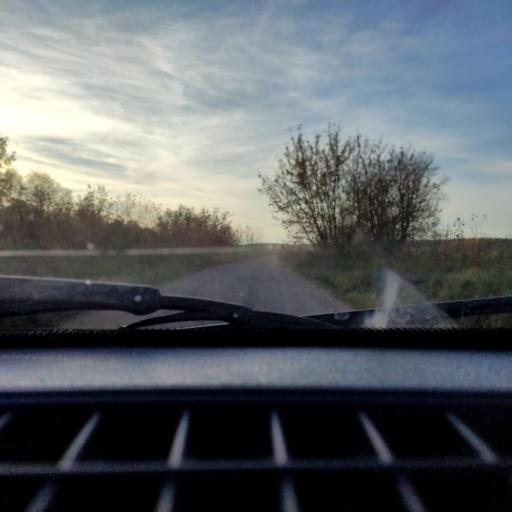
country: RU
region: Bashkortostan
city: Avdon
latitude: 54.6346
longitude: 55.7280
